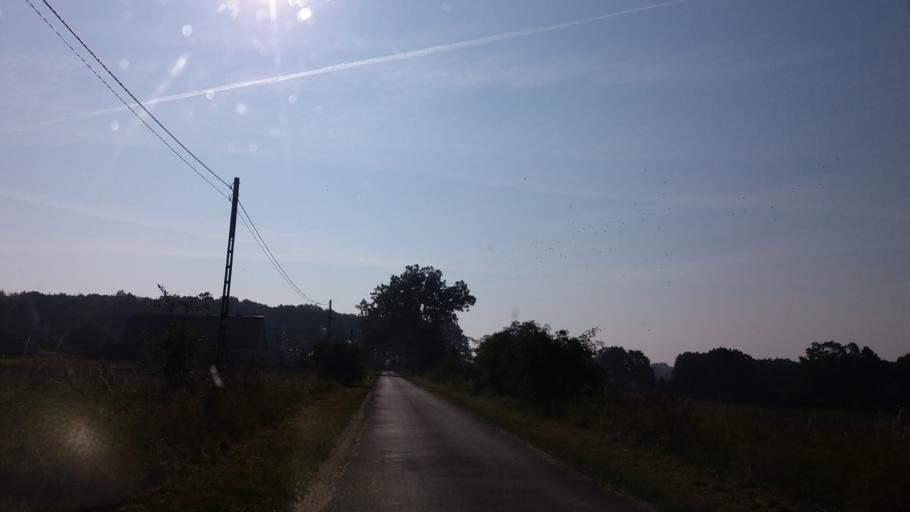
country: PL
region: West Pomeranian Voivodeship
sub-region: Powiat choszczenski
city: Pelczyce
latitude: 53.0005
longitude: 15.3639
